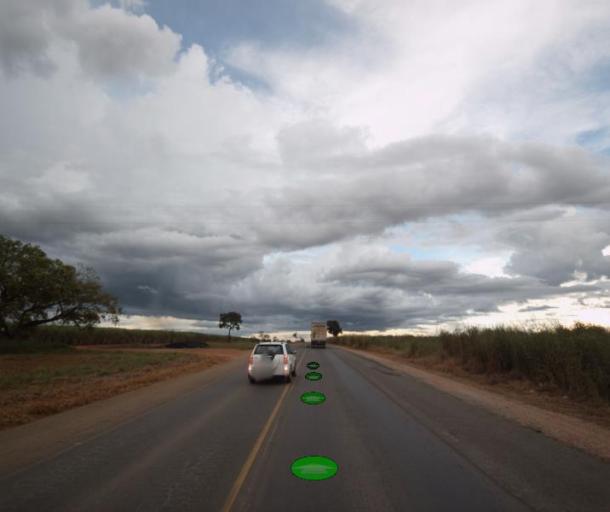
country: BR
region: Goias
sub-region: Itapaci
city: Itapaci
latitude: -14.8021
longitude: -49.2859
